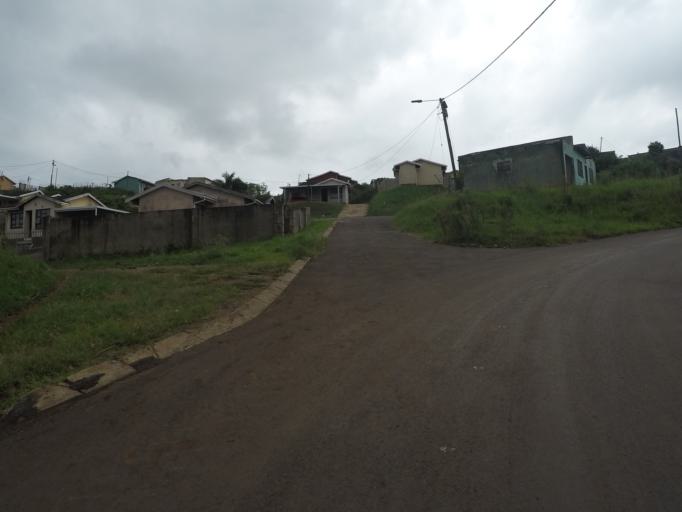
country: ZA
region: KwaZulu-Natal
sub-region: uThungulu District Municipality
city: Empangeni
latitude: -28.7694
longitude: 31.8611
